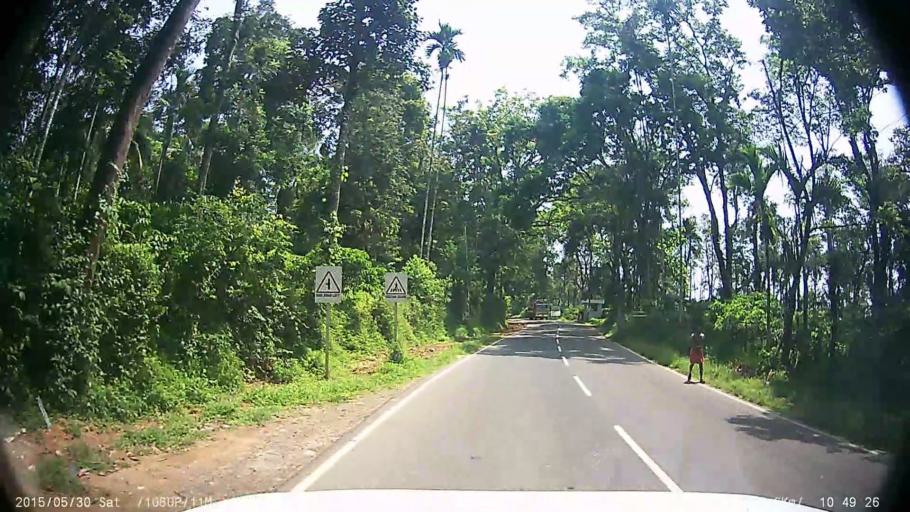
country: IN
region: Kerala
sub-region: Wayanad
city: Kalpetta
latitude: 11.6371
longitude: 76.0859
